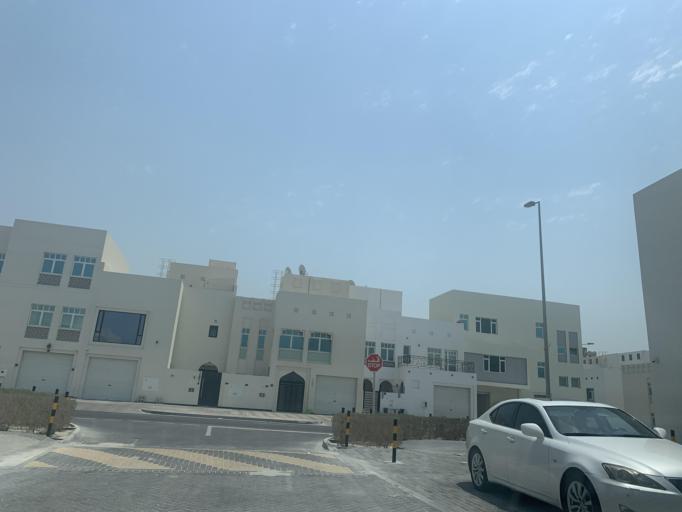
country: BH
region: Muharraq
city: Al Hadd
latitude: 26.2328
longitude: 50.6609
